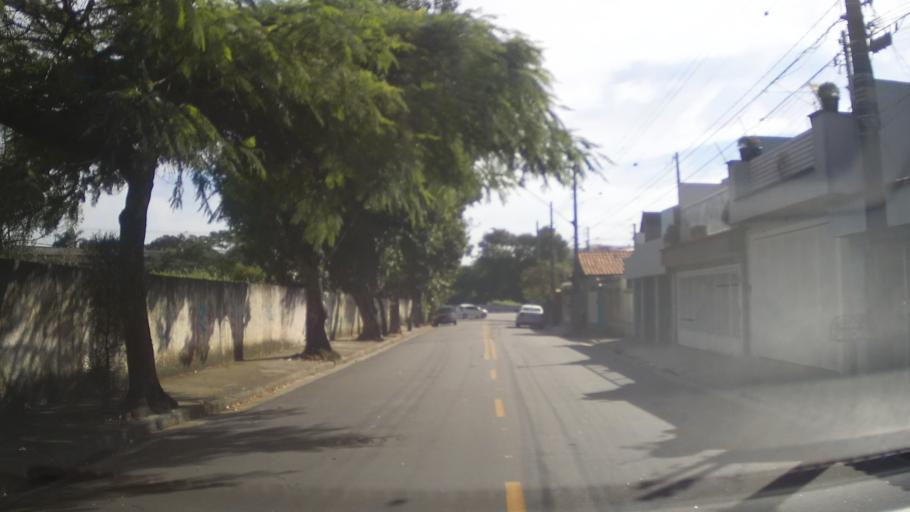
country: BR
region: Sao Paulo
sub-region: Sao Caetano Do Sul
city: Sao Caetano do Sul
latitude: -23.6450
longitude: -46.5777
